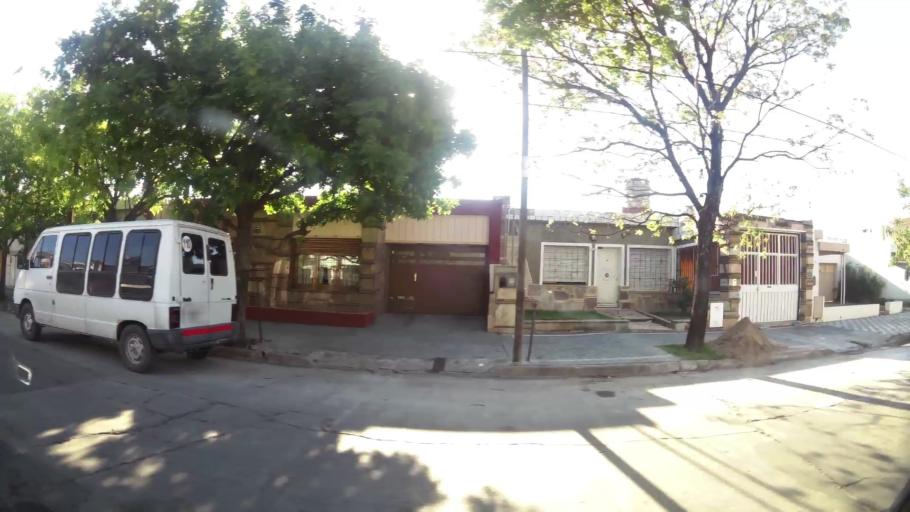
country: AR
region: Cordoba
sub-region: Departamento de Capital
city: Cordoba
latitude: -31.3800
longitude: -64.1772
